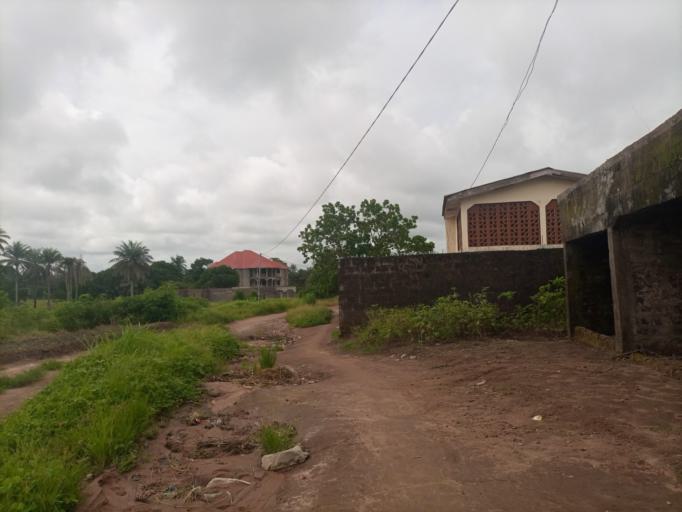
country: SL
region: Northern Province
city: Masoyila
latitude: 8.5960
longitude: -13.1765
